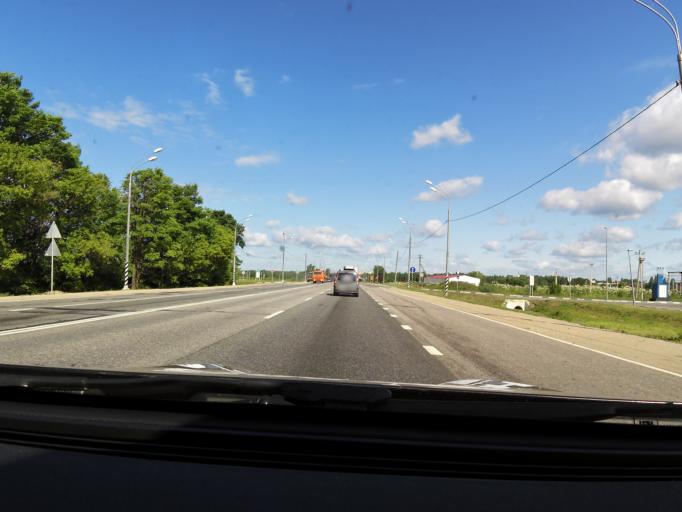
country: RU
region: Tverskaya
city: Tver
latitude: 56.8153
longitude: 35.8299
